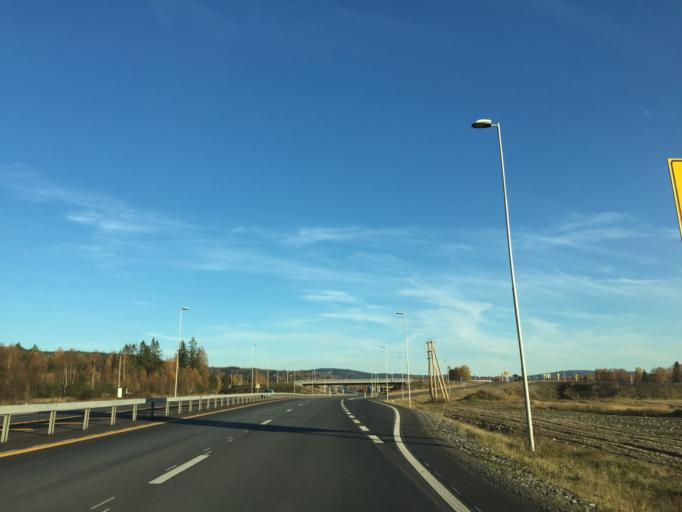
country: NO
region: Hedmark
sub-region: Sor-Odal
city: Skarnes
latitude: 60.2478
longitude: 11.7351
